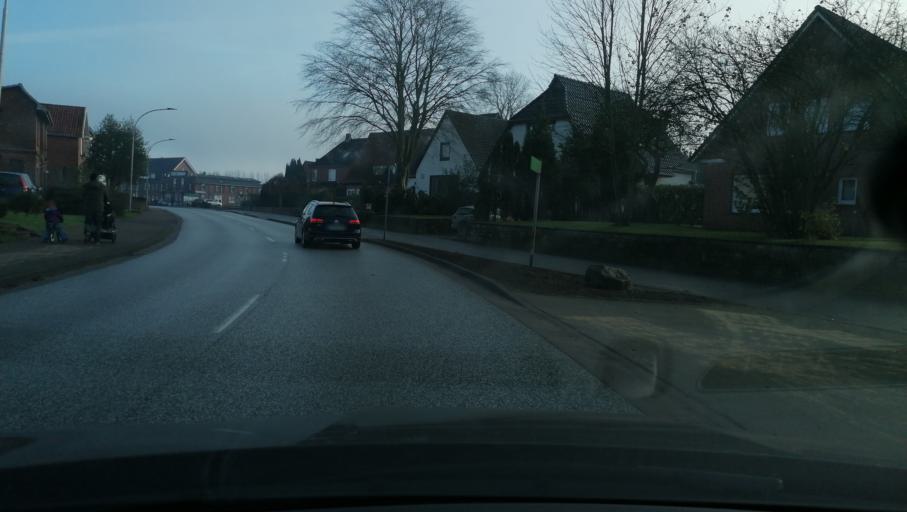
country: DE
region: Schleswig-Holstein
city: Meldorf
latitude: 54.0891
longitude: 9.0844
